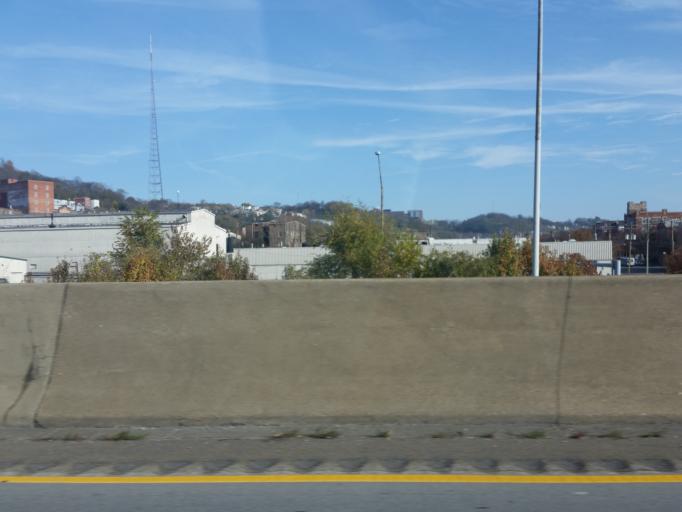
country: US
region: Kentucky
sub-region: Kenton County
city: Ludlow
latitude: 39.1201
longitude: -84.5356
